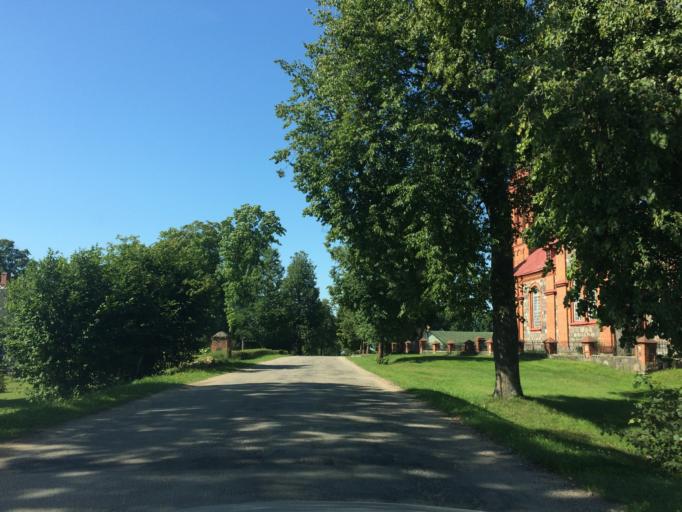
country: LV
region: Rezekne
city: Rezekne
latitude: 56.4926
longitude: 27.1371
